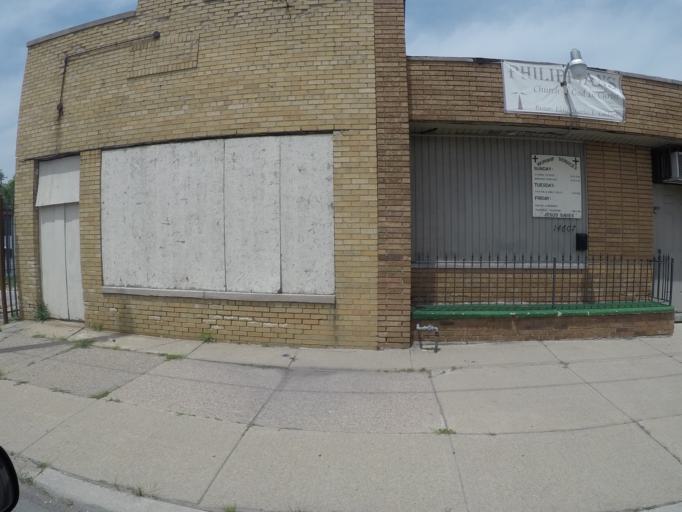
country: US
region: Michigan
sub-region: Macomb County
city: Eastpointe
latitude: 42.4353
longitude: -82.9724
